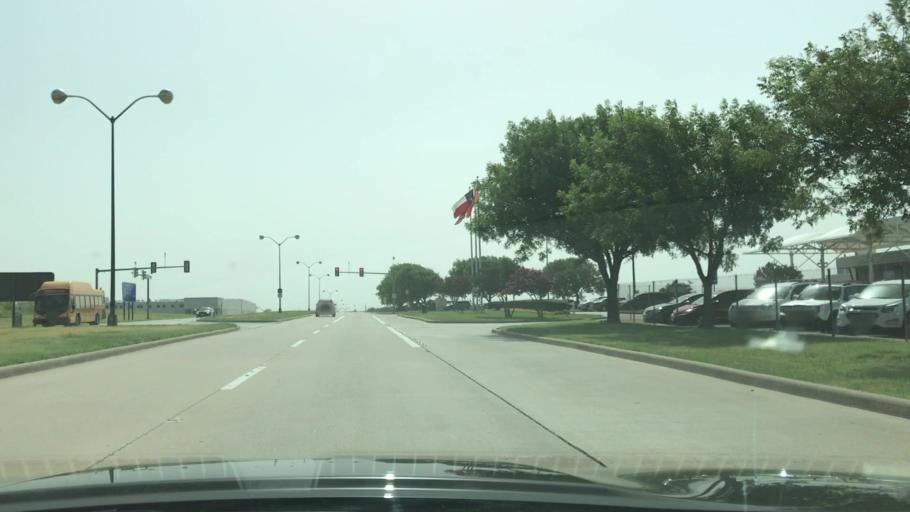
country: US
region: Texas
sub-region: Tarrant County
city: Euless
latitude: 32.8620
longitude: -97.0365
